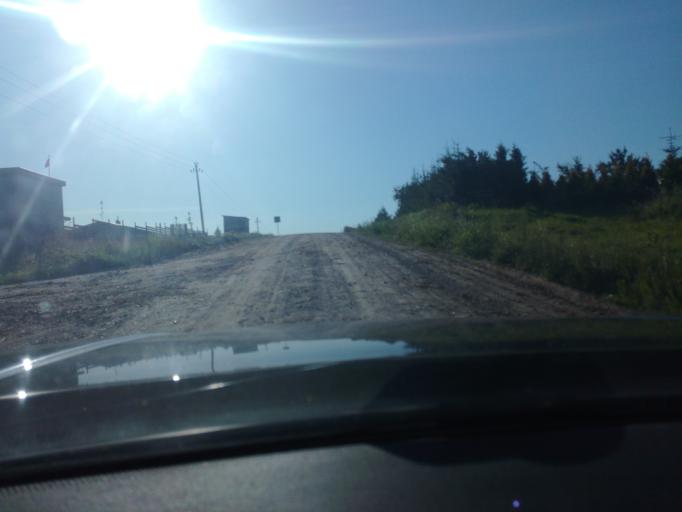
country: LT
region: Alytaus apskritis
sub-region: Alytus
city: Alytus
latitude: 54.4019
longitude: 23.9967
